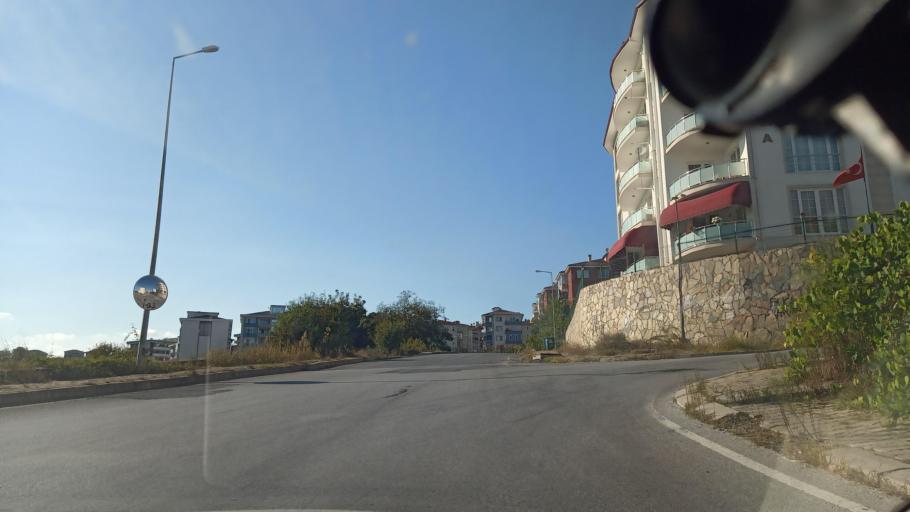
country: TR
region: Sakarya
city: Kazimpasa
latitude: 40.8550
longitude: 30.2915
